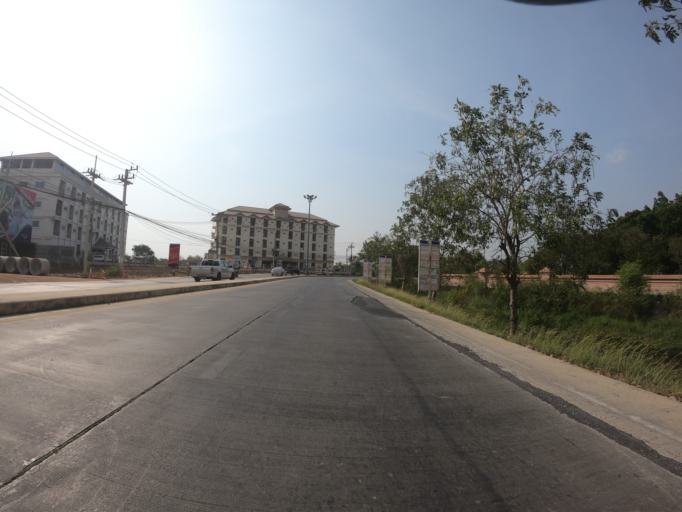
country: TH
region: Phra Nakhon Si Ayutthaya
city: Phra Nakhon Si Ayutthaya
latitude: 14.3411
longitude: 100.5928
